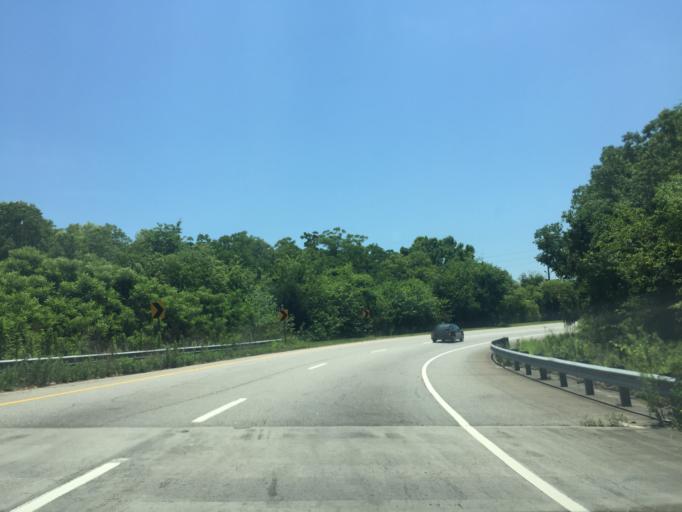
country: US
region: Georgia
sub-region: Chatham County
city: Savannah
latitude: 32.0749
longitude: -81.0717
